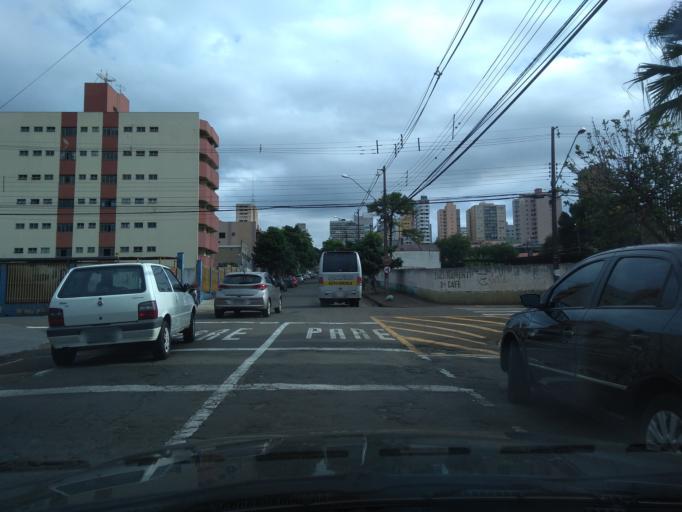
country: BR
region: Parana
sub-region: Londrina
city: Londrina
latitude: -23.3064
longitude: -51.1602
